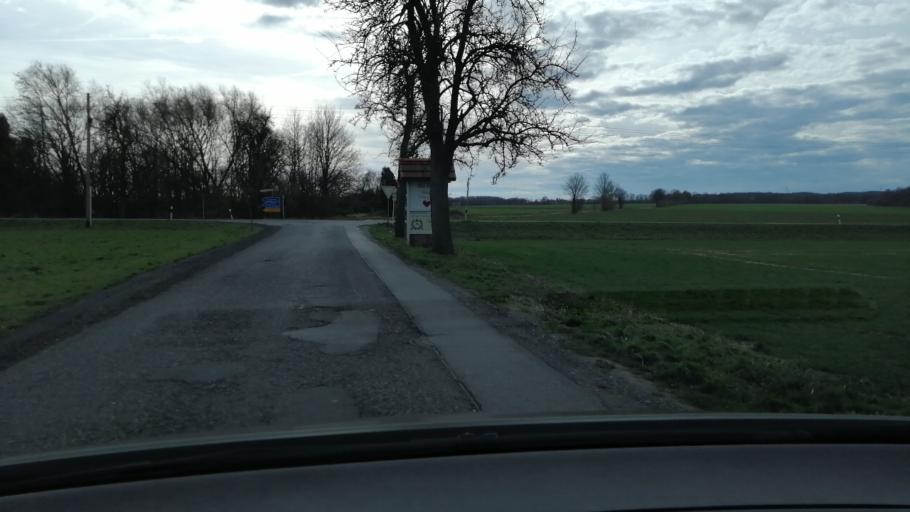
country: DE
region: North Rhine-Westphalia
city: Wickede
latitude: 51.5424
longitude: 7.8483
